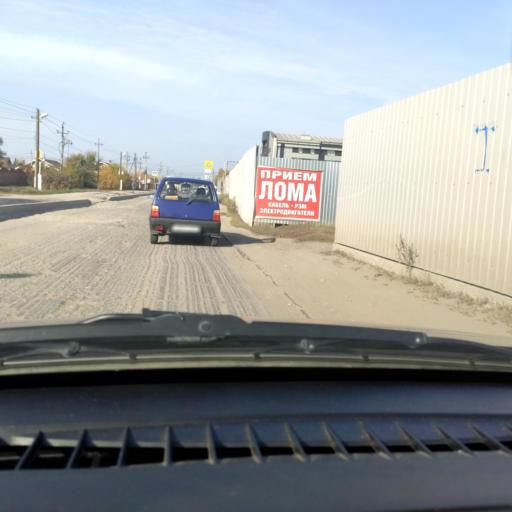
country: RU
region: Samara
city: Tol'yatti
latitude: 53.5097
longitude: 49.2430
